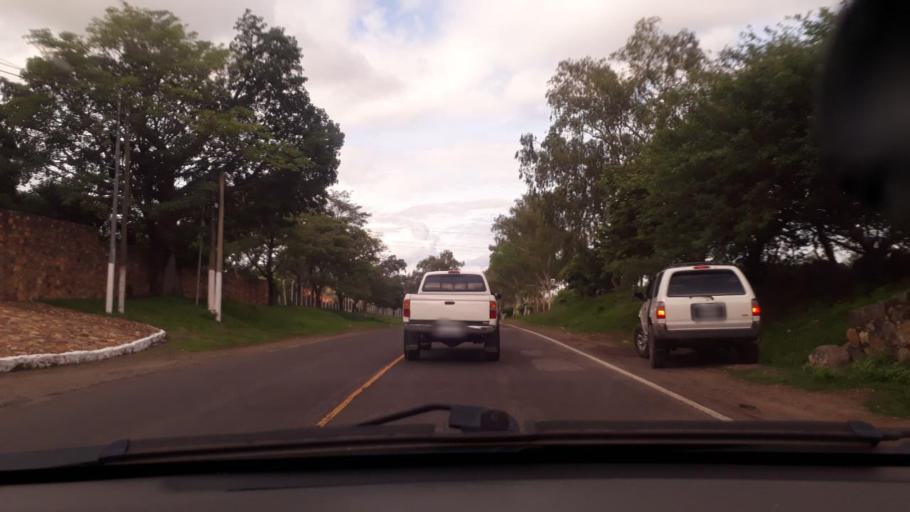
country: GT
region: Jutiapa
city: Jutiapa
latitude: 14.2889
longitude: -89.9349
